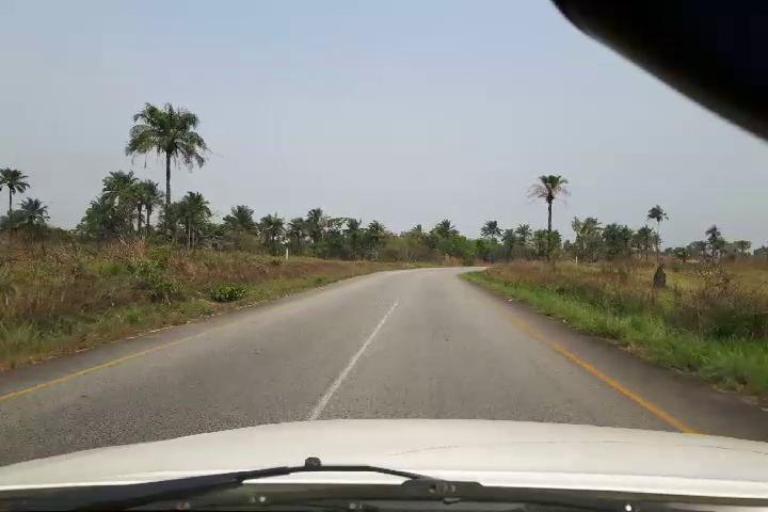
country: SL
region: Southern Province
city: Largo
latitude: 8.3045
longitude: -12.2035
